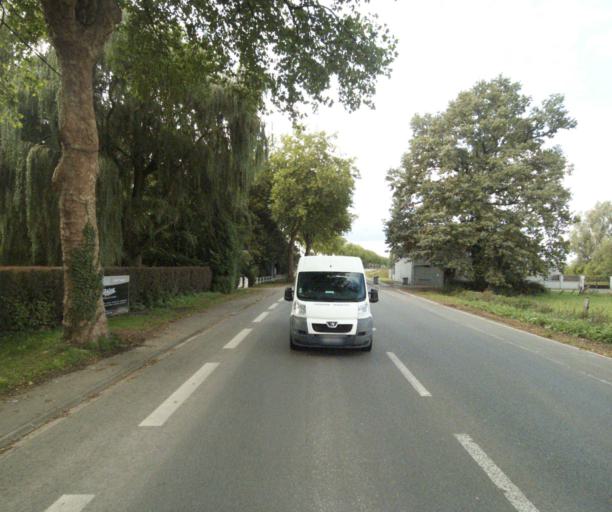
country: FR
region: Nord-Pas-de-Calais
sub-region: Departement du Nord
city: Premesques
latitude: 50.6527
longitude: 2.9399
